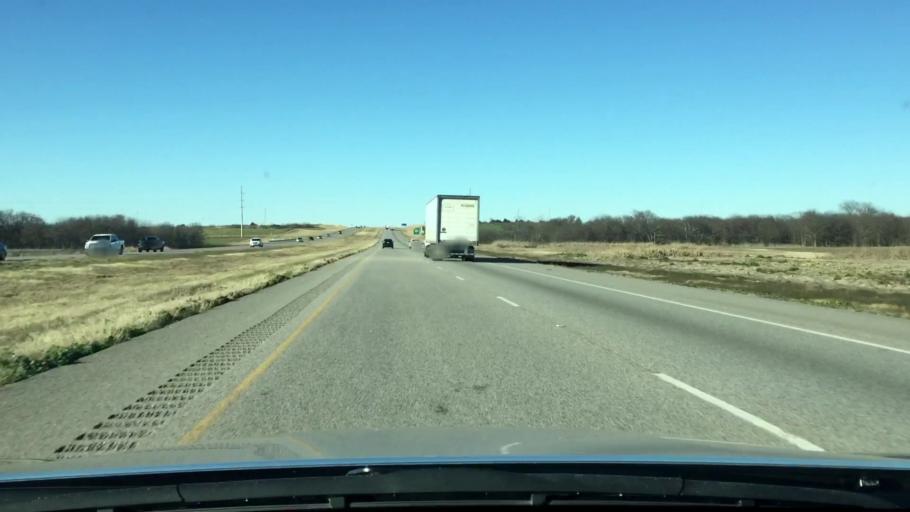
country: US
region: Texas
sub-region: Hill County
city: Itasca
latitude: 32.1325
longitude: -97.1198
